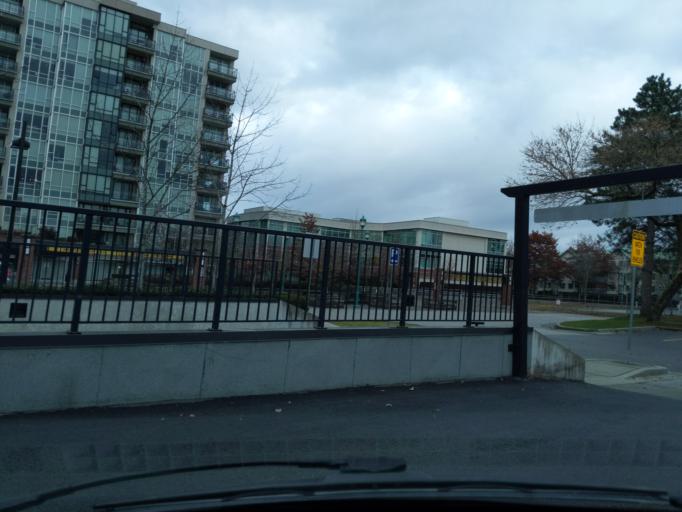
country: CA
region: British Columbia
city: Pitt Meadows
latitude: 49.2214
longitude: -122.6910
